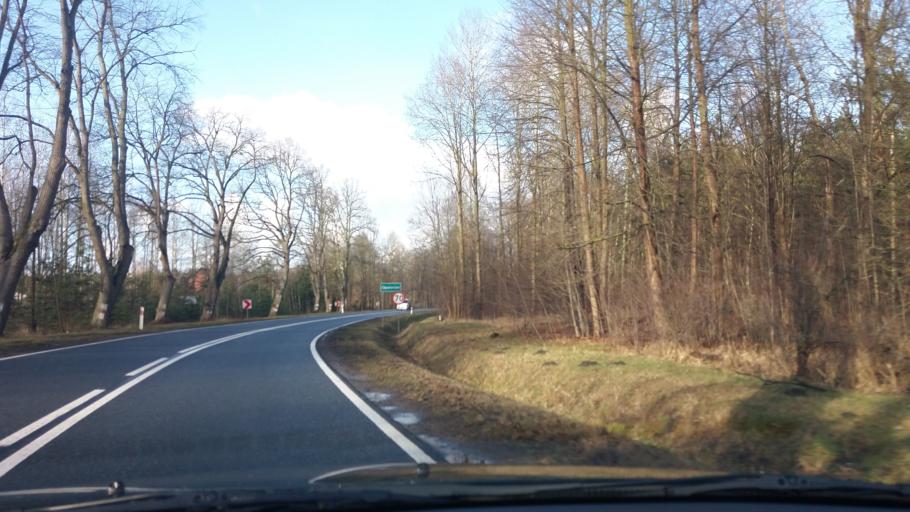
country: PL
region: Masovian Voivodeship
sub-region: Powiat przasnyski
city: Chorzele
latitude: 53.2796
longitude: 20.8984
